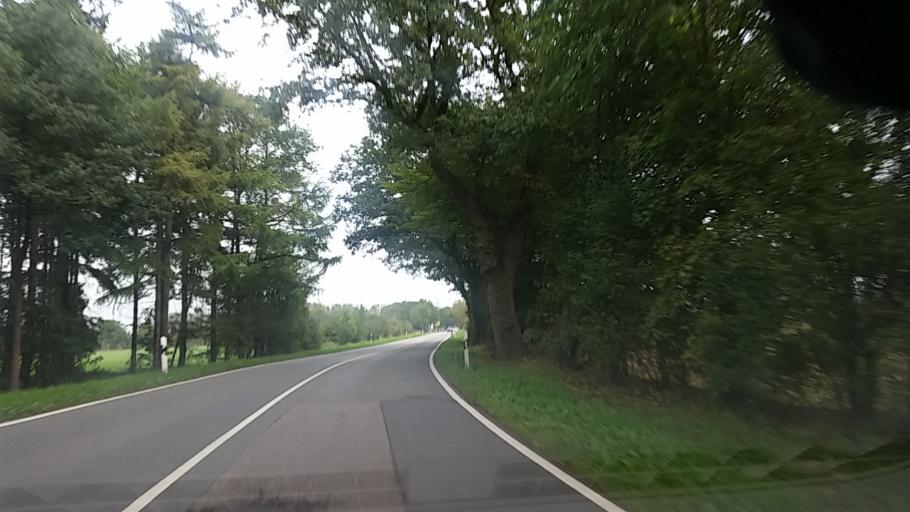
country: DE
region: Schleswig-Holstein
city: Hasenmoor
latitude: 53.8935
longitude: 9.9785
